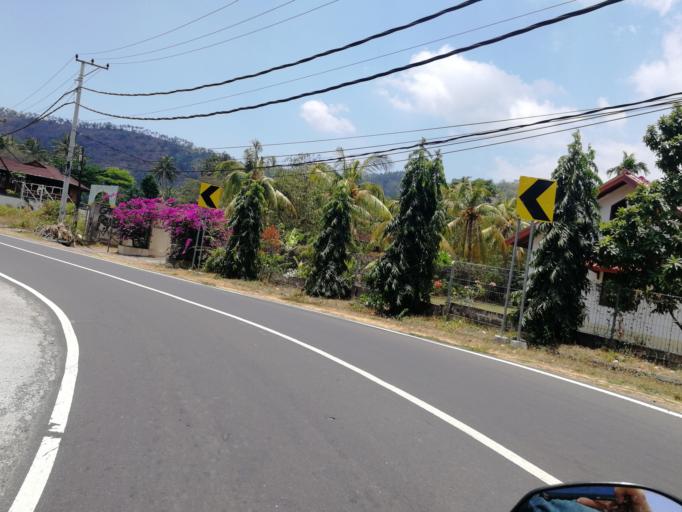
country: ID
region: West Nusa Tenggara
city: Karangsubagan
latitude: -8.4601
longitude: 116.0381
